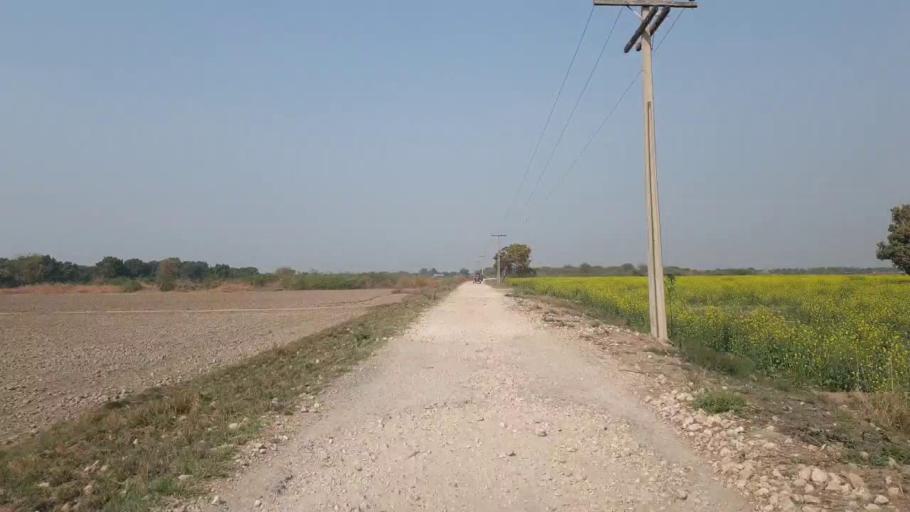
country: PK
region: Sindh
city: Mirwah Gorchani
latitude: 25.3789
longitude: 68.9477
